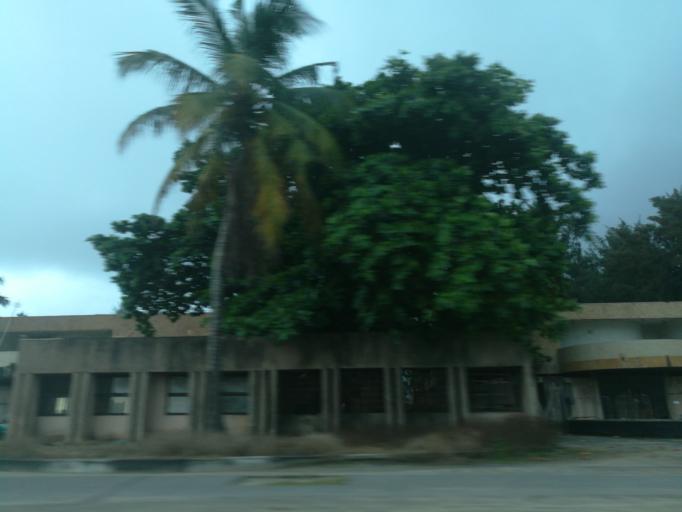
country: NG
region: Lagos
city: Ikoyi
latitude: 6.4225
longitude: 3.4164
